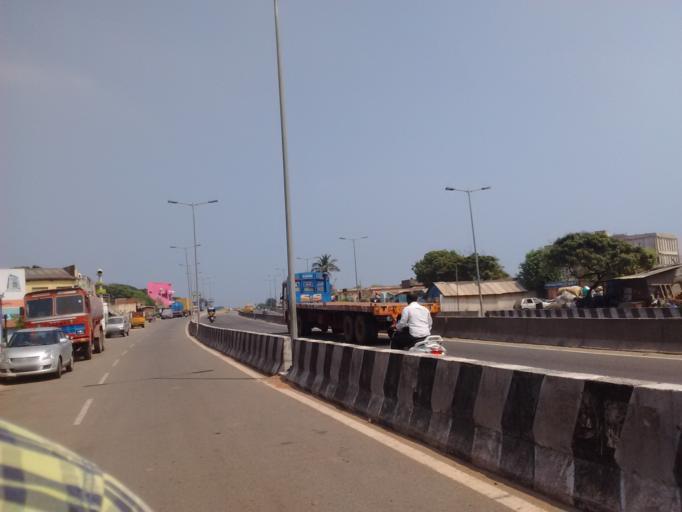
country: IN
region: Tamil Nadu
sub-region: Thiruvallur
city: Tiruvottiyur
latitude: 13.1661
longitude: 80.3077
